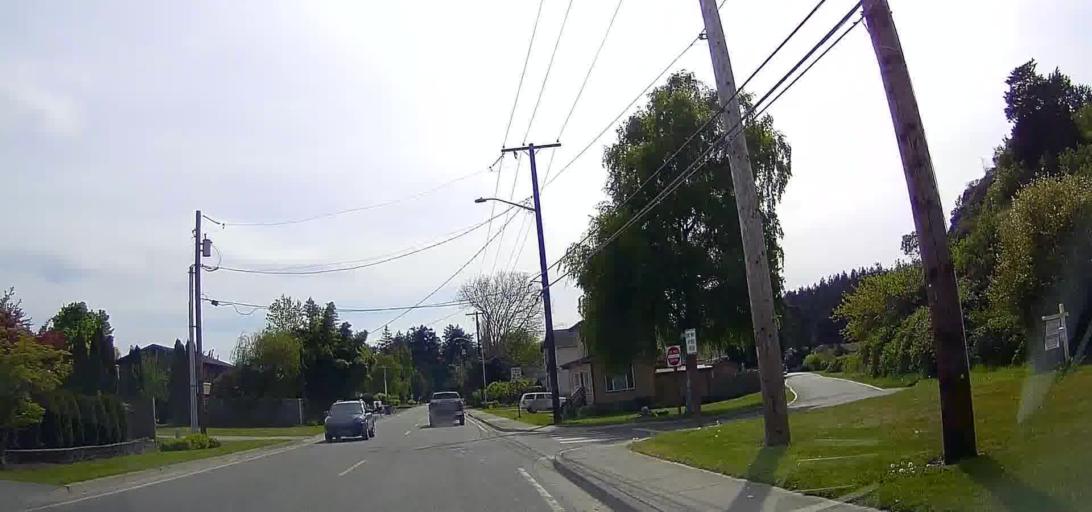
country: US
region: Washington
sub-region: Skagit County
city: Mount Vernon
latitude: 48.3879
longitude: -122.4928
